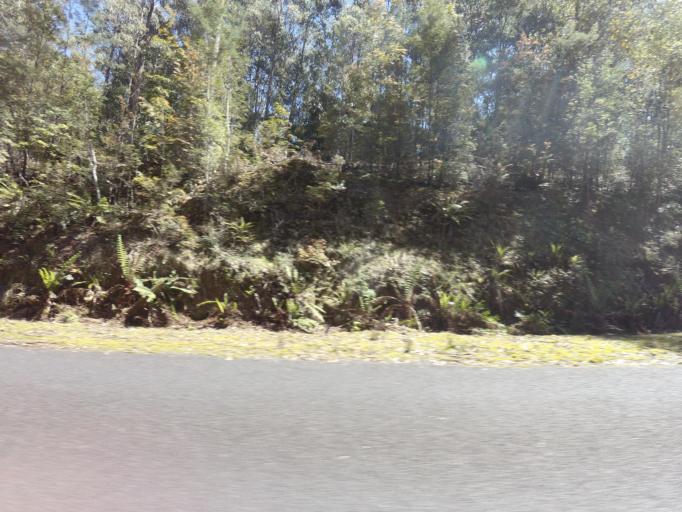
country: AU
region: Tasmania
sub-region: Huon Valley
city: Geeveston
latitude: -42.8196
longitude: 146.3414
